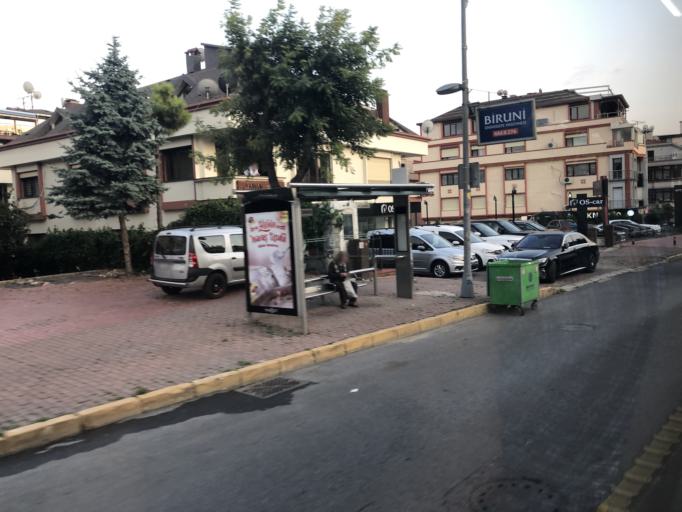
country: TR
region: Istanbul
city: Bahcelievler
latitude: 40.9781
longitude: 28.7920
